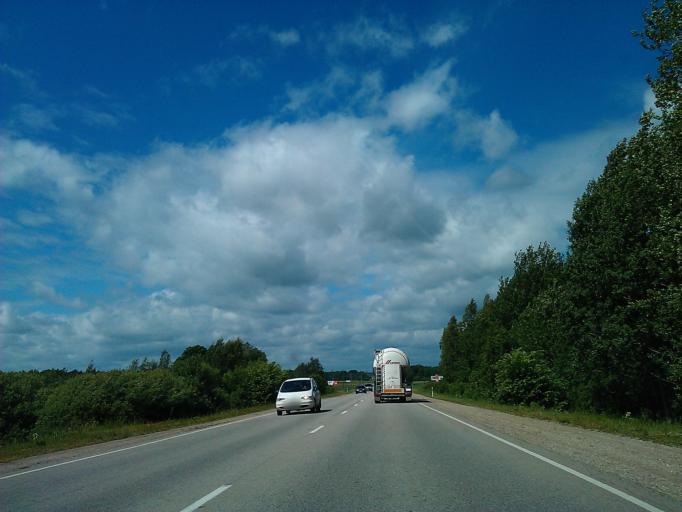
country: LV
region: Tukuma Rajons
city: Tukums
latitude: 56.9473
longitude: 23.1293
